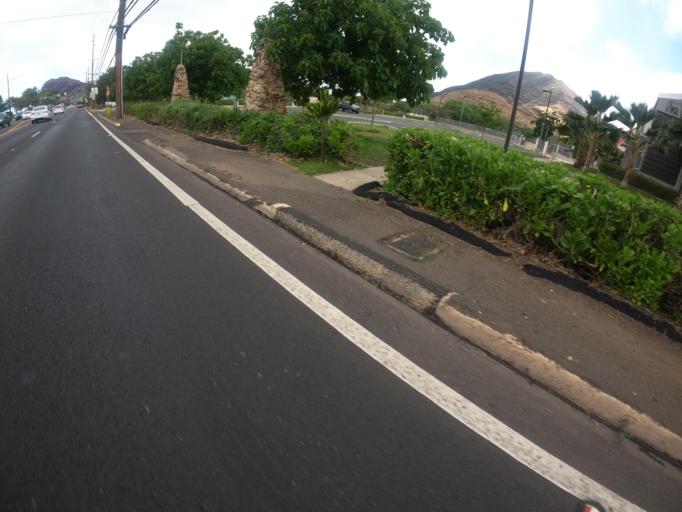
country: US
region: Hawaii
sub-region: Honolulu County
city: Nanakuli
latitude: 21.3820
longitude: -158.1460
